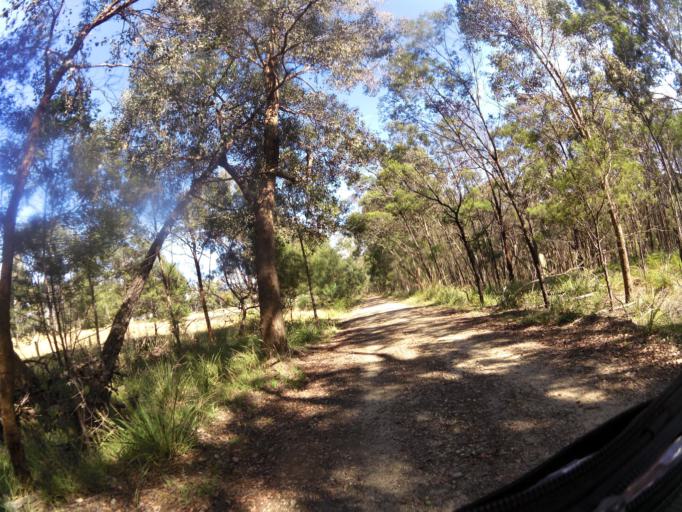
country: AU
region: Victoria
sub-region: East Gippsland
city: Lakes Entrance
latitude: -37.7463
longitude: 148.1765
